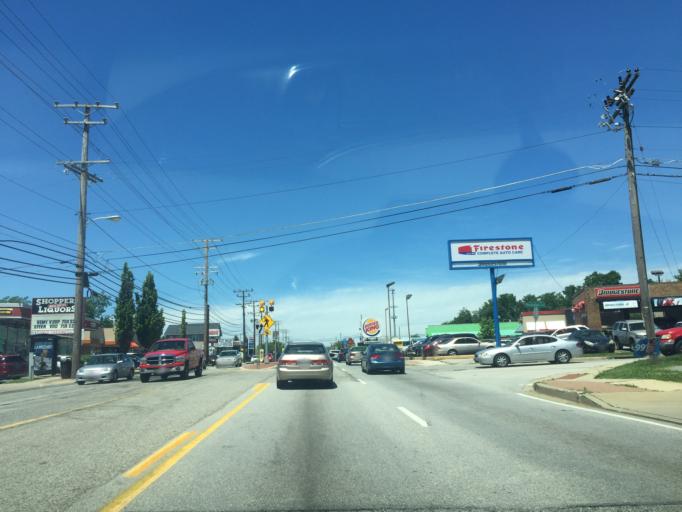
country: US
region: Maryland
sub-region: Baltimore County
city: Milford Mill
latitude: 39.3526
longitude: -76.7549
